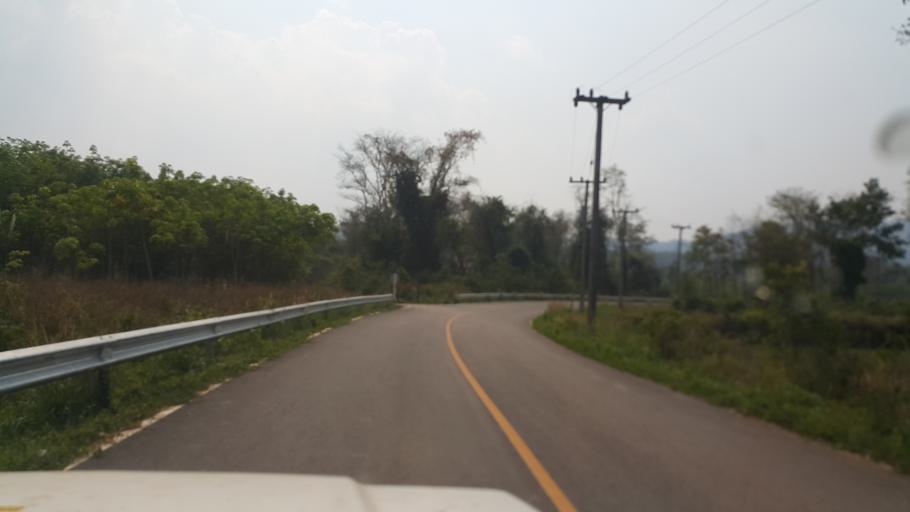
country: TH
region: Nakhon Phanom
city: Ban Phaeng
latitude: 17.9514
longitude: 104.1698
